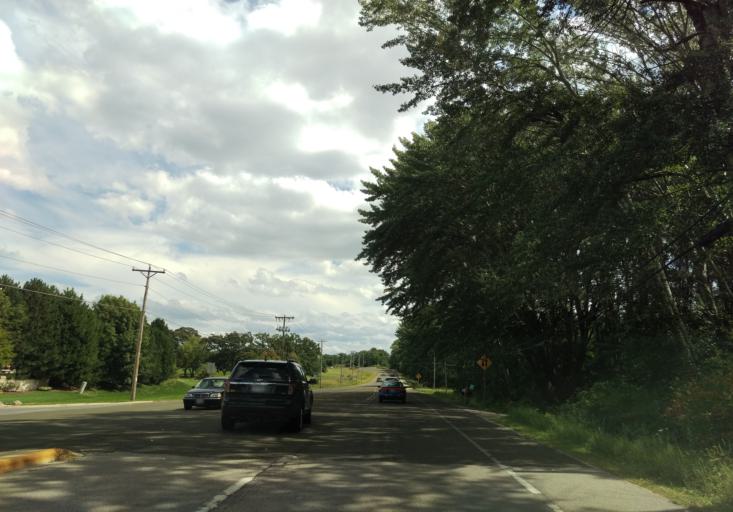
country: US
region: Wisconsin
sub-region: Dane County
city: Shorewood Hills
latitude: 43.1119
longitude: -89.4649
